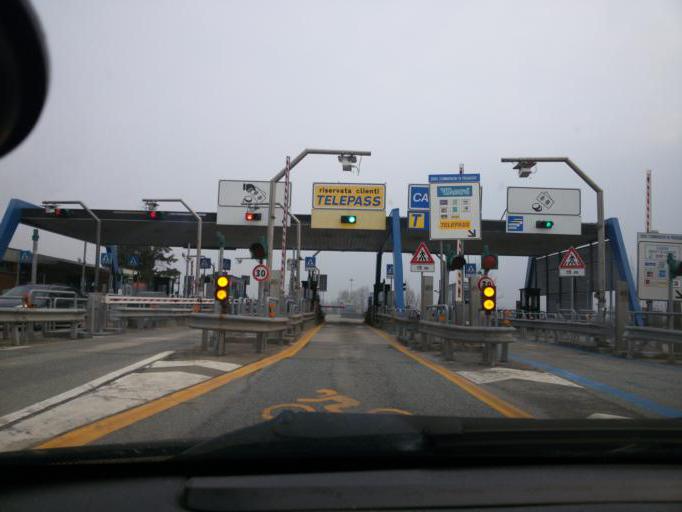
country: IT
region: Piedmont
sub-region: Provincia di Vercelli
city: Asigliano Vercellese
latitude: 45.2942
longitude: 8.3891
